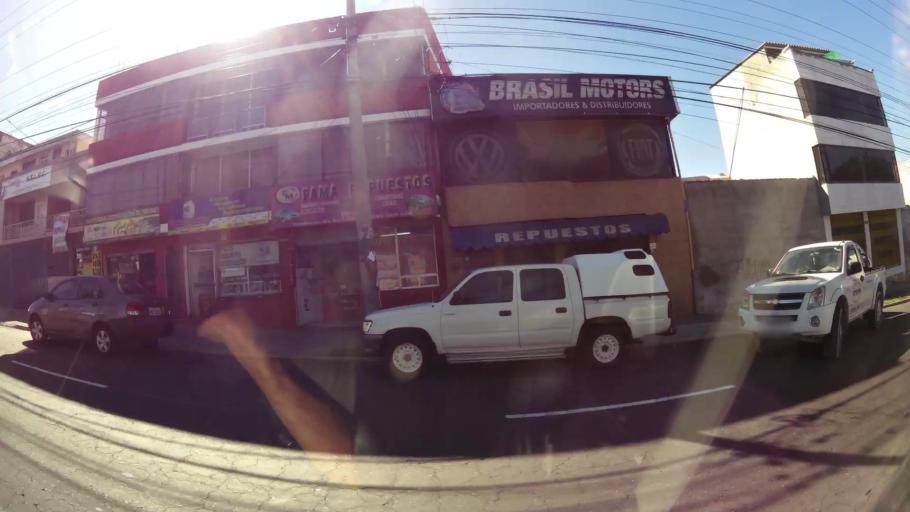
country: EC
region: Pichincha
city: Quito
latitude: -0.1379
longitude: -78.4733
